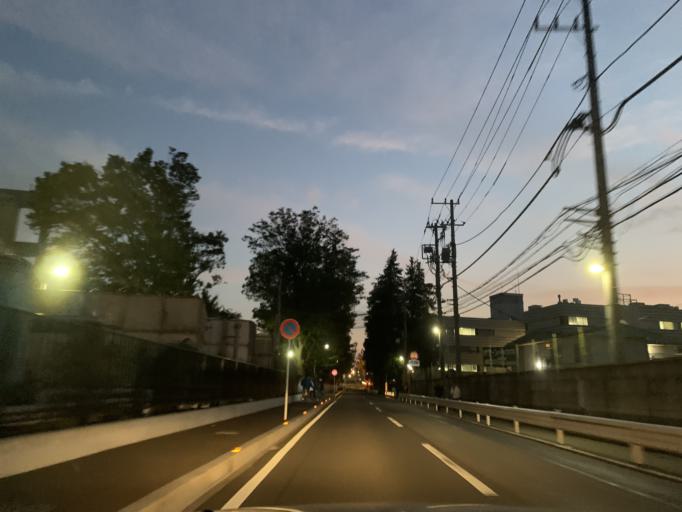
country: JP
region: Chiba
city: Noda
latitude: 35.9189
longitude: 139.9067
